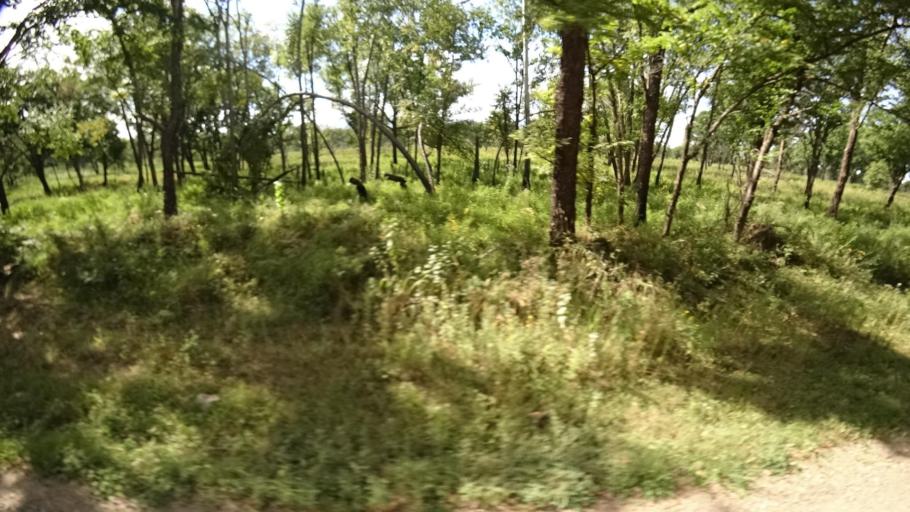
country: RU
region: Primorskiy
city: Yakovlevka
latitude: 44.3981
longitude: 133.5616
